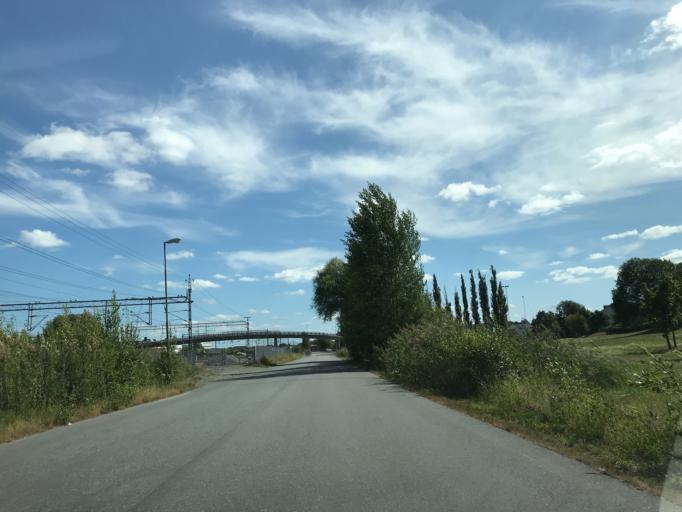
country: SE
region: Stockholm
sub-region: Upplands Vasby Kommun
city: Upplands Vaesby
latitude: 59.4806
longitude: 17.9096
